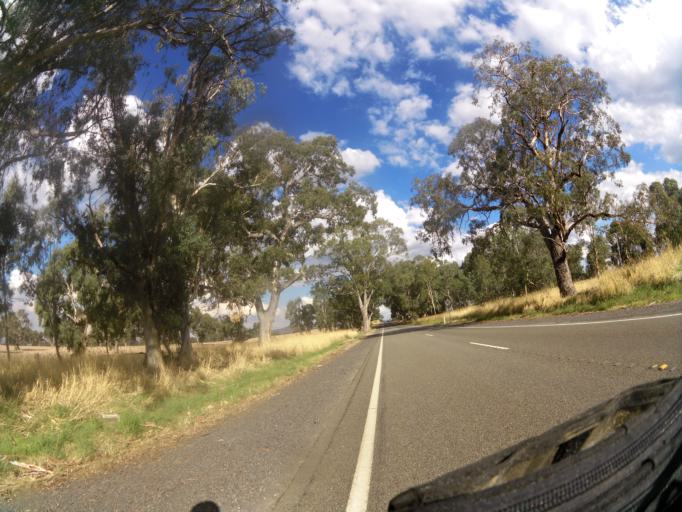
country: AU
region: Victoria
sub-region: Mansfield
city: Mansfield
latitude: -37.0127
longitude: 146.0863
